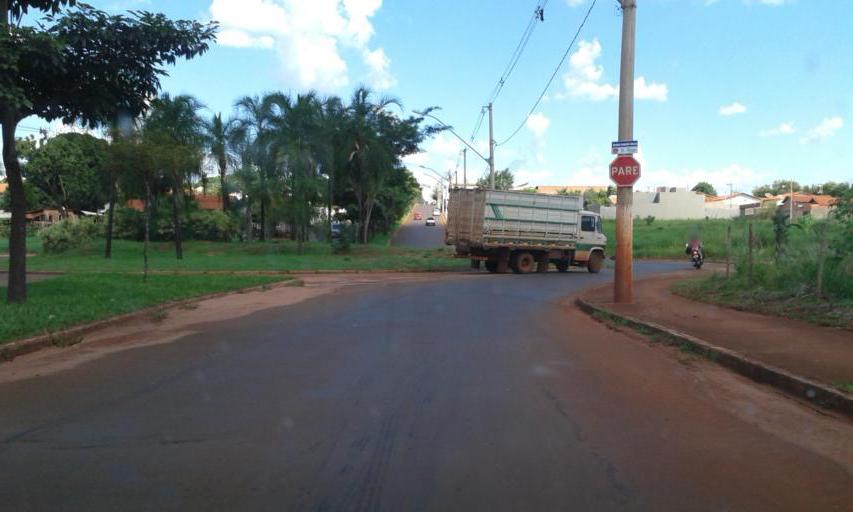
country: BR
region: Minas Gerais
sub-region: Ituiutaba
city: Ituiutaba
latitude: -18.9693
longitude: -49.4885
